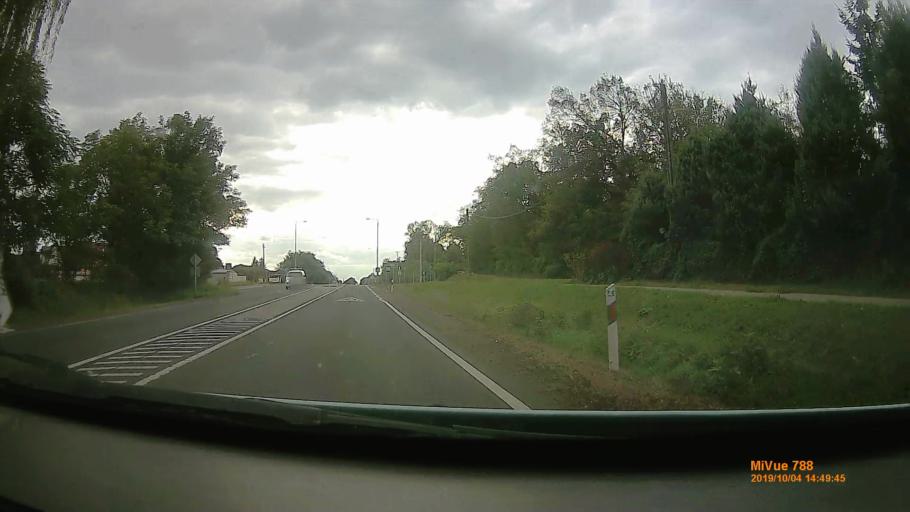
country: HU
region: Szabolcs-Szatmar-Bereg
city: Nyirpazony
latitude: 47.9845
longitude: 21.7865
